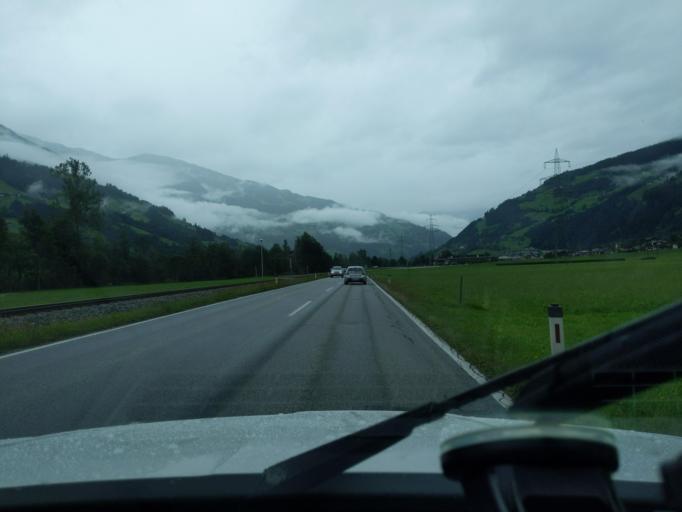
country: AT
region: Tyrol
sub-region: Politischer Bezirk Schwaz
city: Schwendau
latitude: 47.1854
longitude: 11.8663
